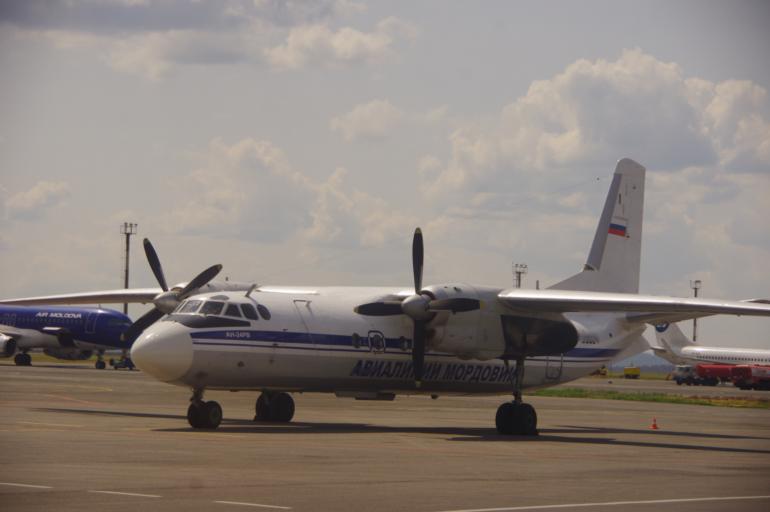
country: RU
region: Samara
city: Bereza
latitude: 53.5079
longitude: 50.1463
